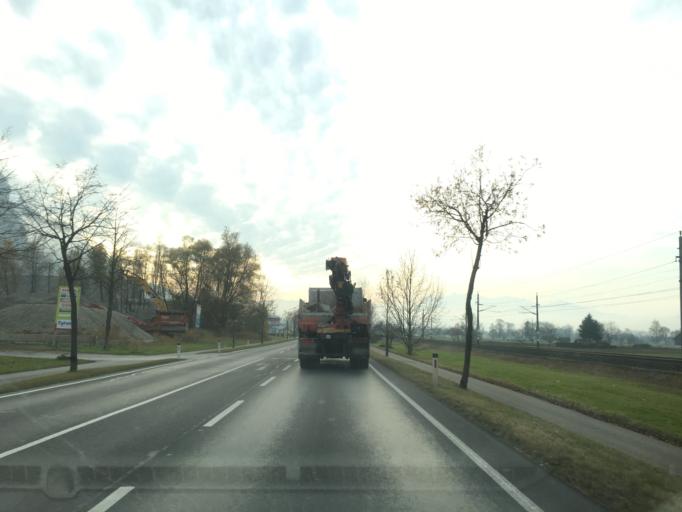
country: AT
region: Vorarlberg
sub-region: Politischer Bezirk Dornbirn
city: Hohenems
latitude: 47.3785
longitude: 9.7022
